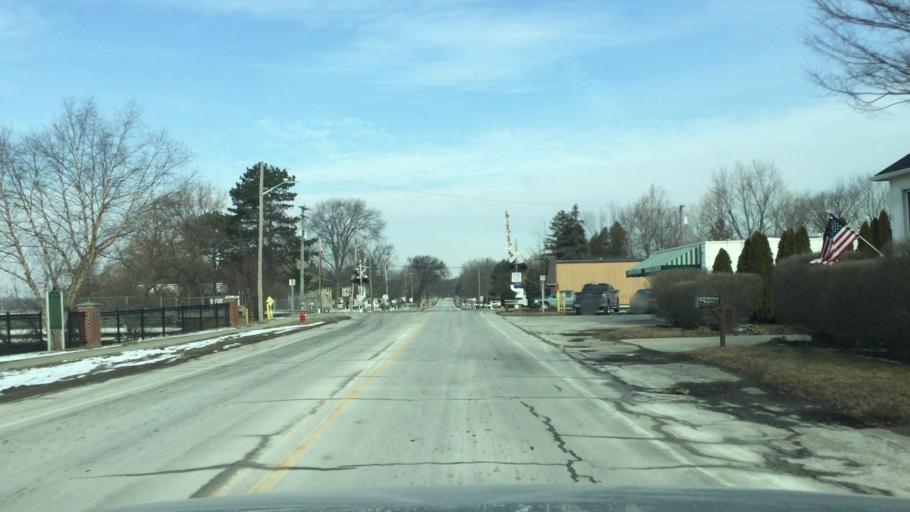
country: US
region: Michigan
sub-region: Wayne County
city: Flat Rock
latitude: 42.0998
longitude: -83.2942
